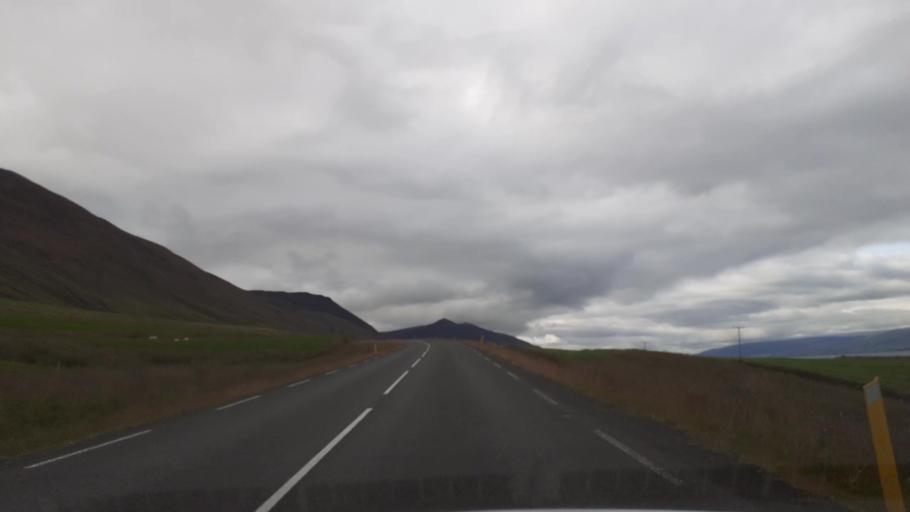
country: IS
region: Northeast
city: Akureyri
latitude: 65.8650
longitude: -18.0734
